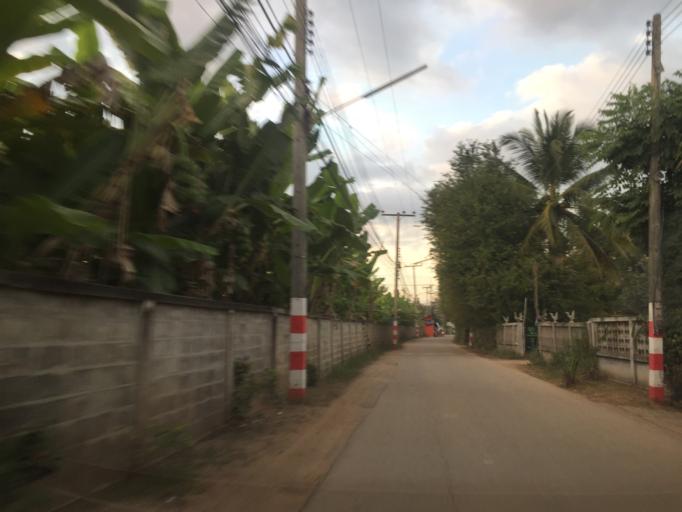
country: TH
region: Lamphun
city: Lamphun
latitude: 18.5249
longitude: 99.0174
